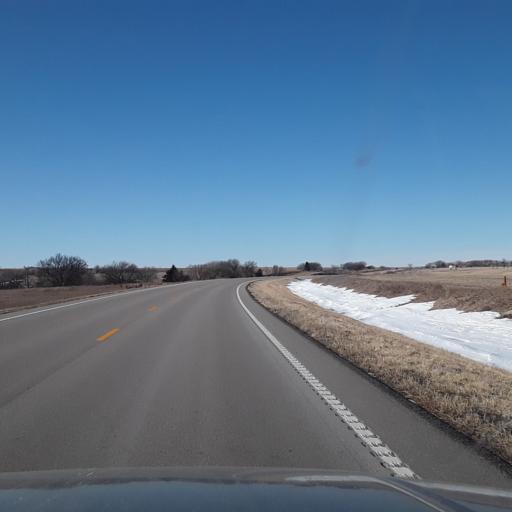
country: US
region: Nebraska
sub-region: Dawson County
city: Cozad
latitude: 40.6712
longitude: -100.1025
